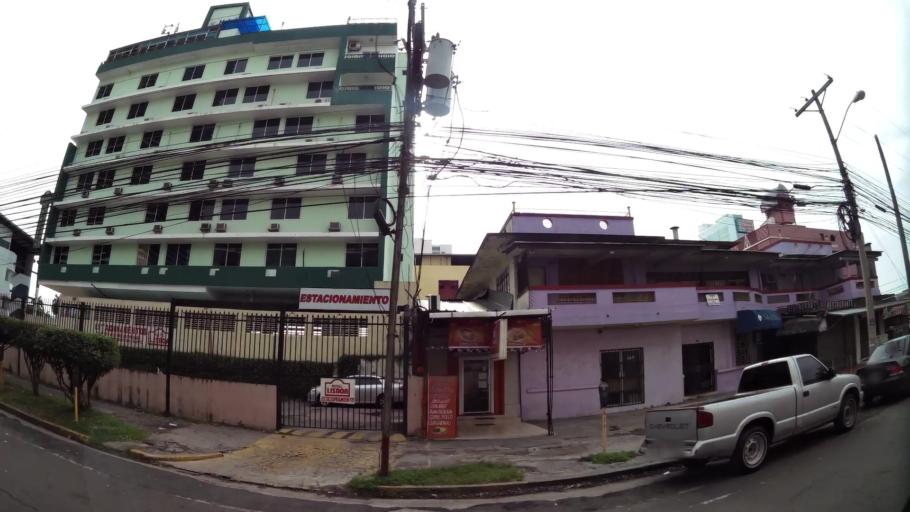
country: PA
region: Panama
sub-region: Distrito de Panama
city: Ancon
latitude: 8.9675
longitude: -79.5371
